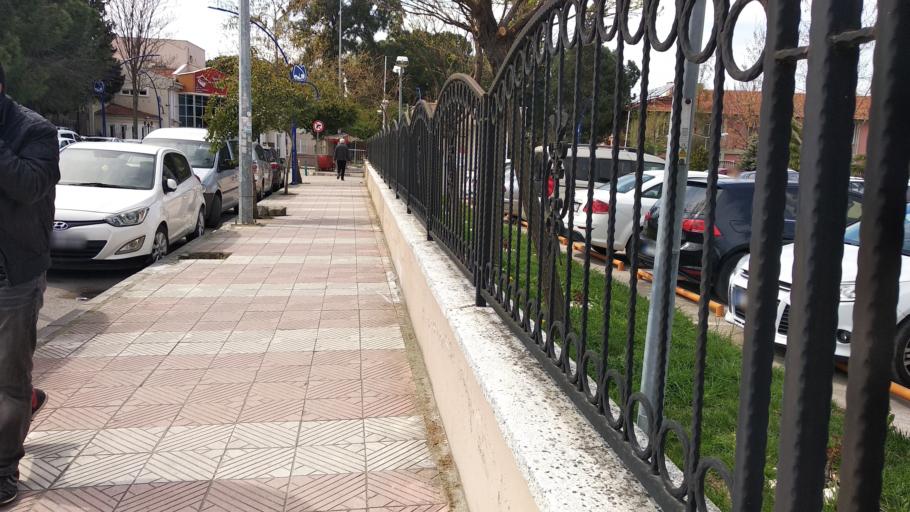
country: TR
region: Manisa
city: Manisa
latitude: 38.6150
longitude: 27.4179
